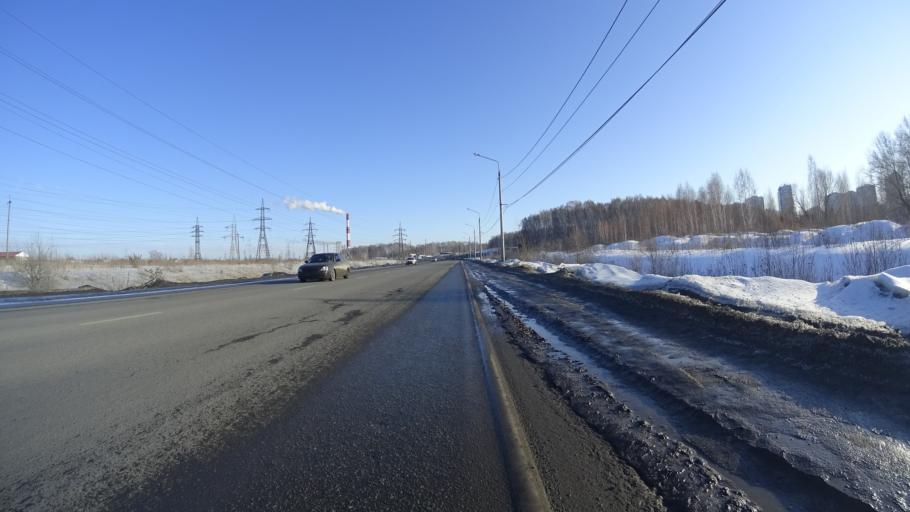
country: RU
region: Chelyabinsk
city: Roshchino
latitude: 55.2131
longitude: 61.3066
